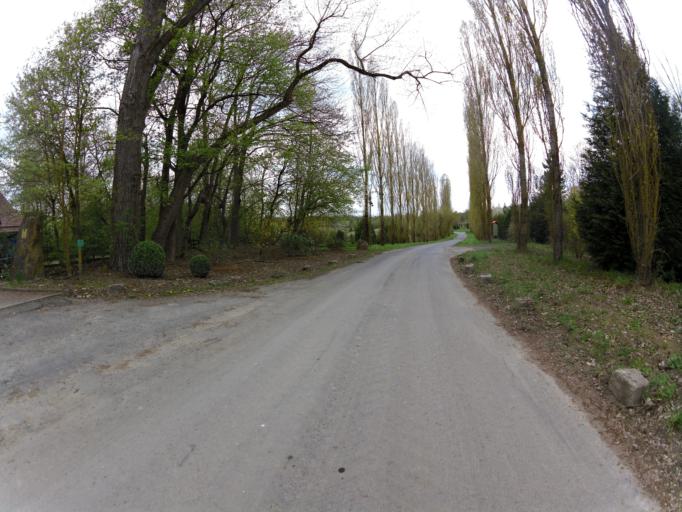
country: DE
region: Bavaria
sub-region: Regierungsbezirk Unterfranken
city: Hettstadt
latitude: 49.8184
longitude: 9.7949
